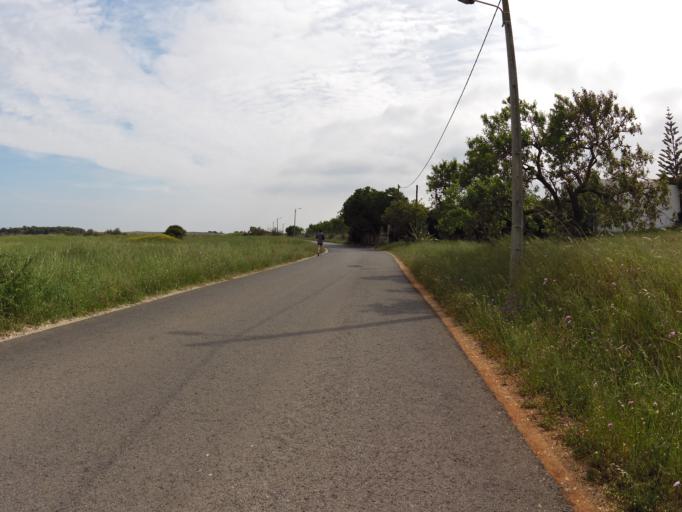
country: PT
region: Faro
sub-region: Silves
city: Armacao de Pera
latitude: 37.1109
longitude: -8.3489
